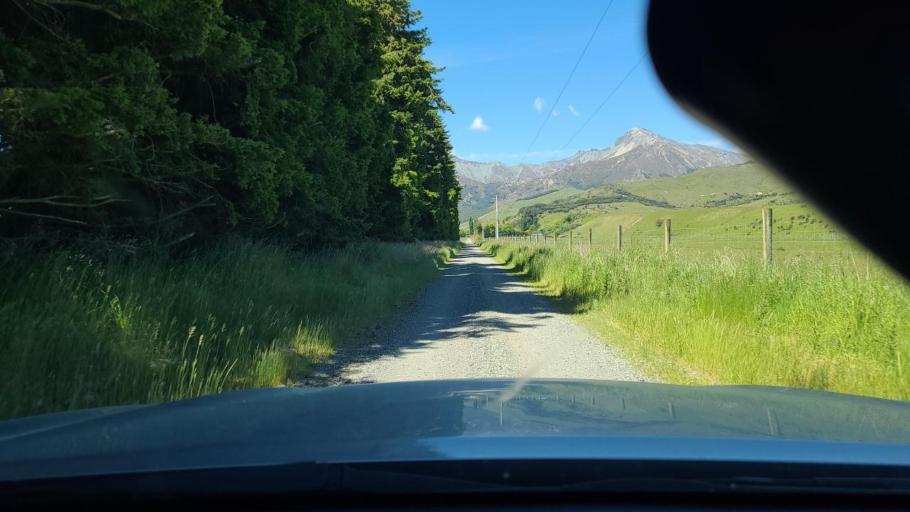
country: NZ
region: Southland
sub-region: Southland District
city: Te Anau
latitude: -45.5621
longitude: 167.8855
